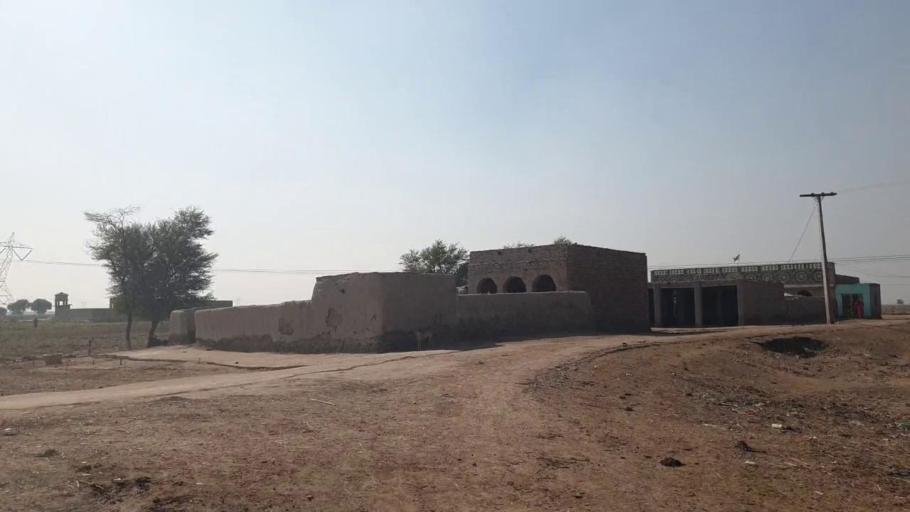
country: PK
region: Sindh
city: Sehwan
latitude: 26.4232
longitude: 67.8112
